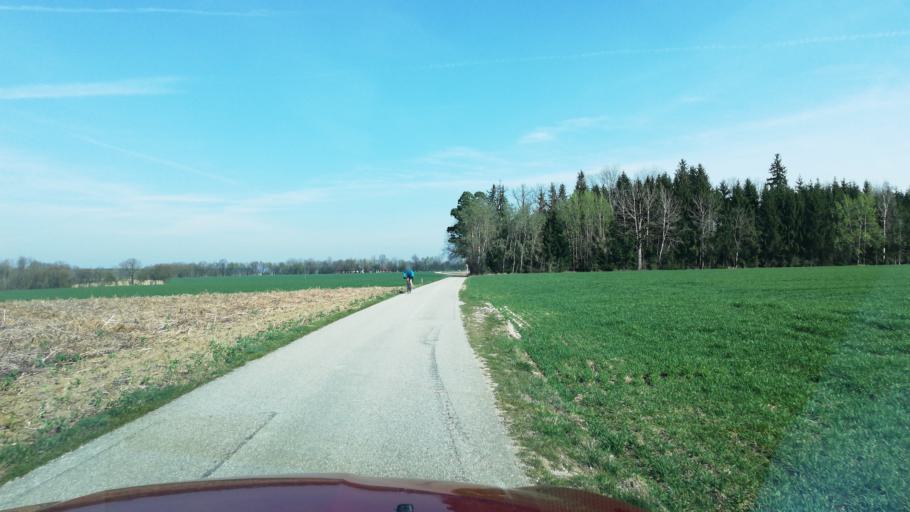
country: AT
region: Upper Austria
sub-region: Wels-Land
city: Sattledt
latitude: 48.1119
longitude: 14.0718
